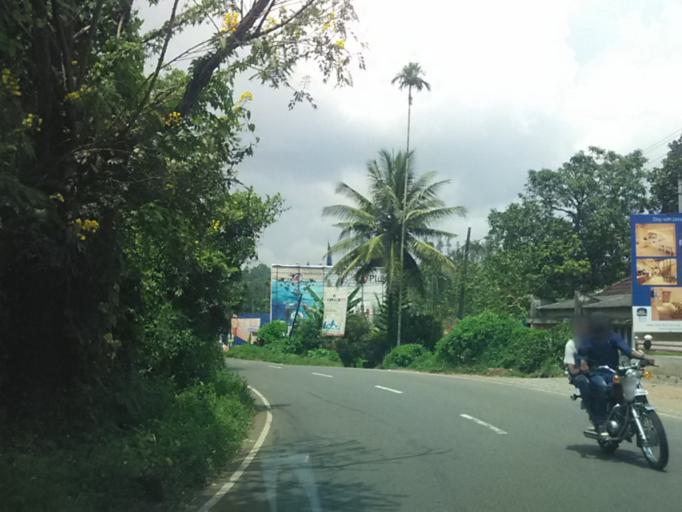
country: IN
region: Kerala
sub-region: Wayanad
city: Kalpetta
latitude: 11.5765
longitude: 76.0597
